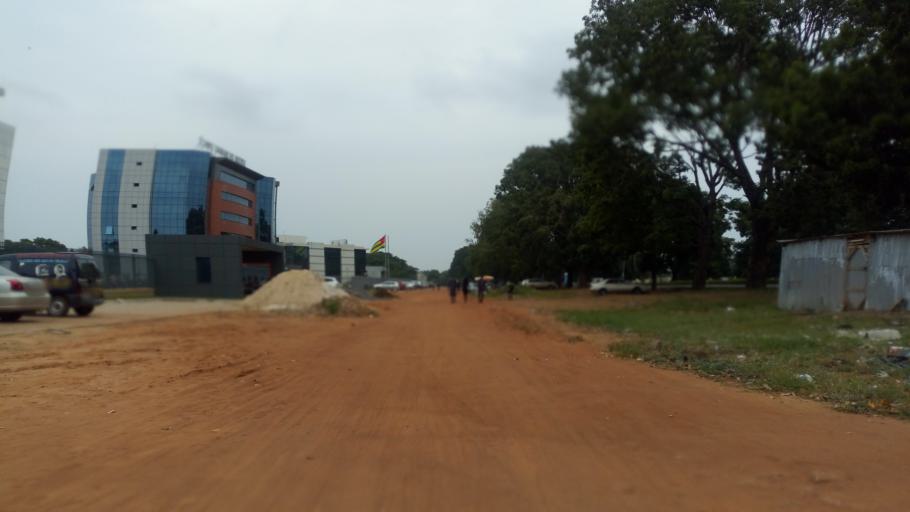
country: TG
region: Maritime
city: Lome
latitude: 6.1877
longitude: 1.2120
